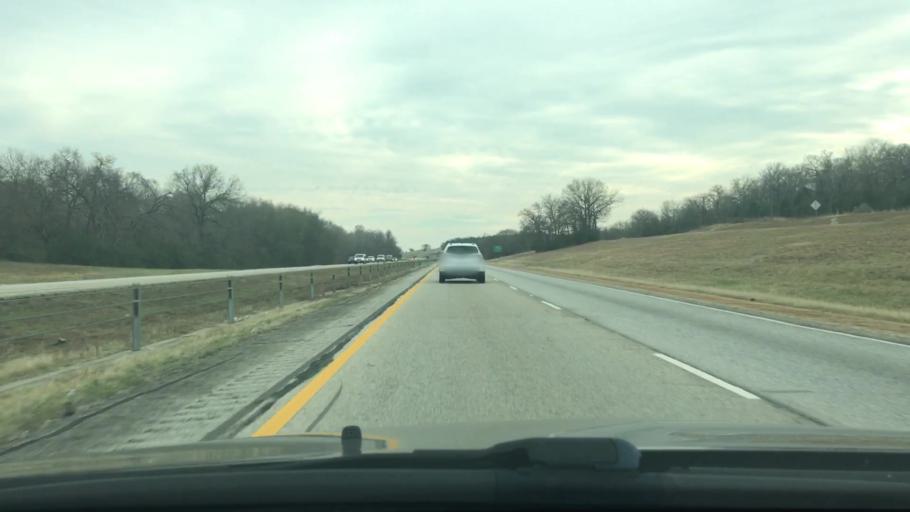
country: US
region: Texas
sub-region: Leon County
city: Centerville
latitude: 31.3018
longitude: -96.0002
